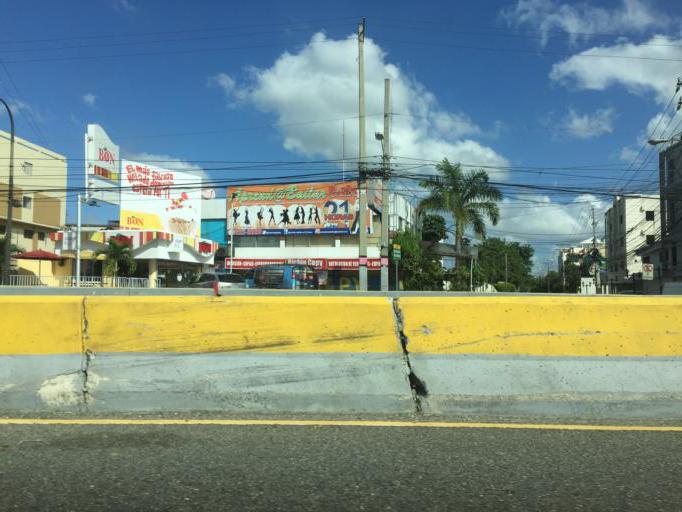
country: DO
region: Nacional
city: San Carlos
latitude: 18.4762
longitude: -69.9114
